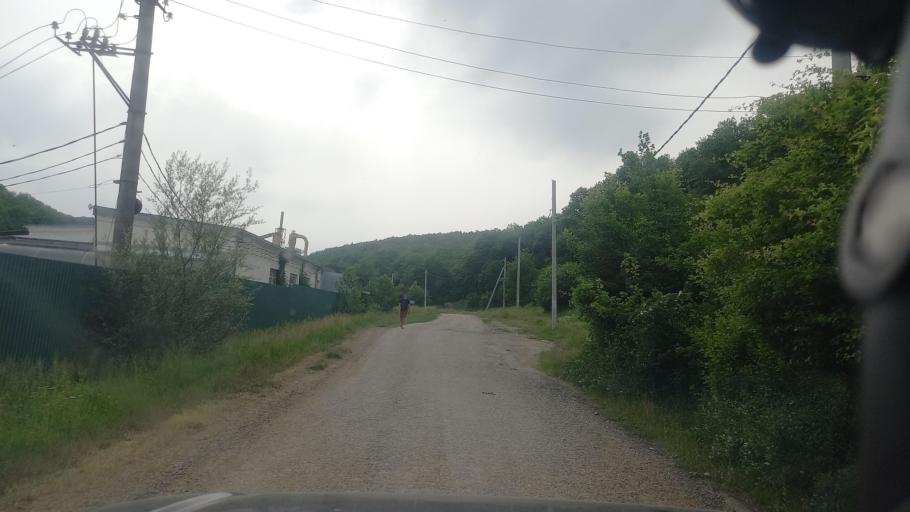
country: RU
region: Krasnodarskiy
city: Goryachiy Klyuch
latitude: 44.6055
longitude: 38.9925
